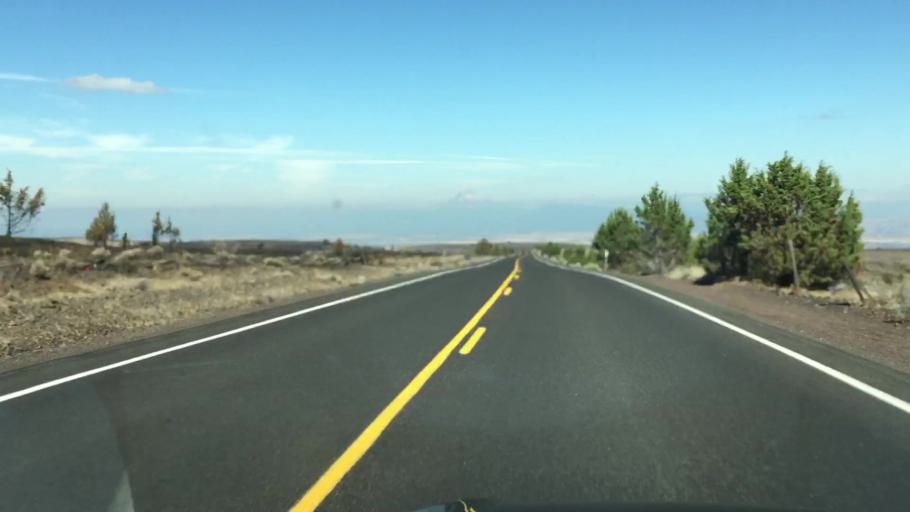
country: US
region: Oregon
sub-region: Jefferson County
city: Warm Springs
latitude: 45.0542
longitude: -121.0170
